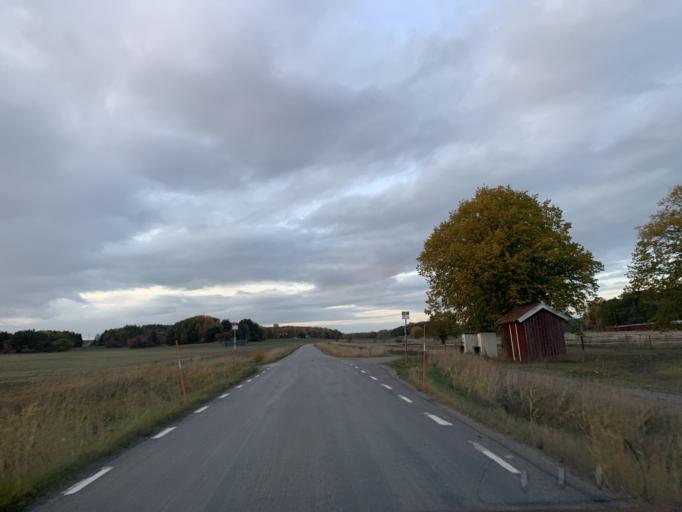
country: SE
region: Stockholm
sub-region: Nynashamns Kommun
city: Osmo
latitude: 58.9060
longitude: 17.7885
